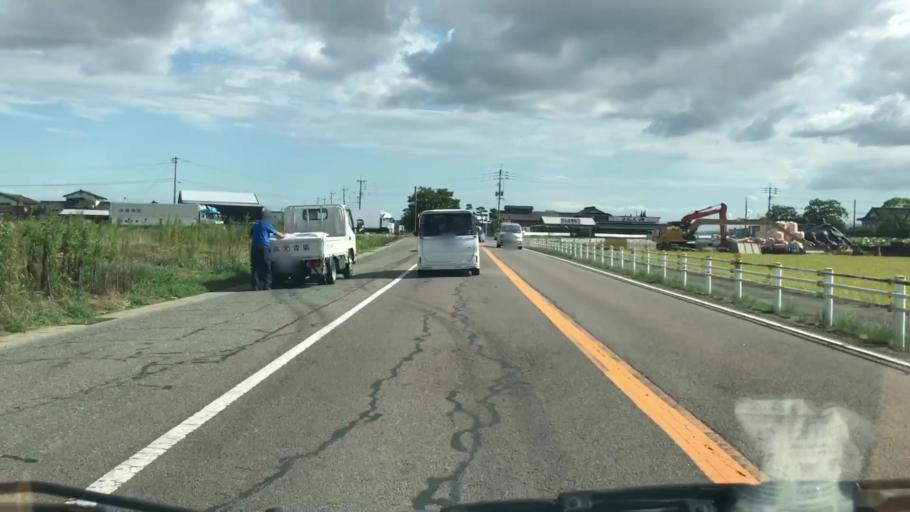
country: JP
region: Saga Prefecture
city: Kashima
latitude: 33.1711
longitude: 130.1808
